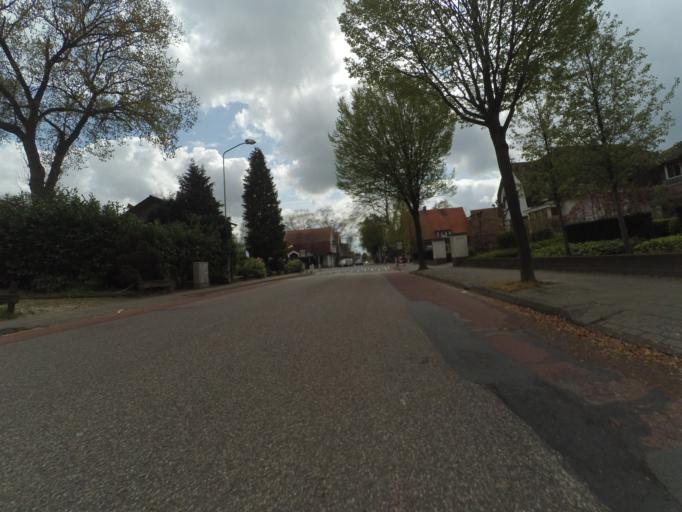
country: NL
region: Gelderland
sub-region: Gemeente Ede
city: Lunteren
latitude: 52.0907
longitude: 5.6185
